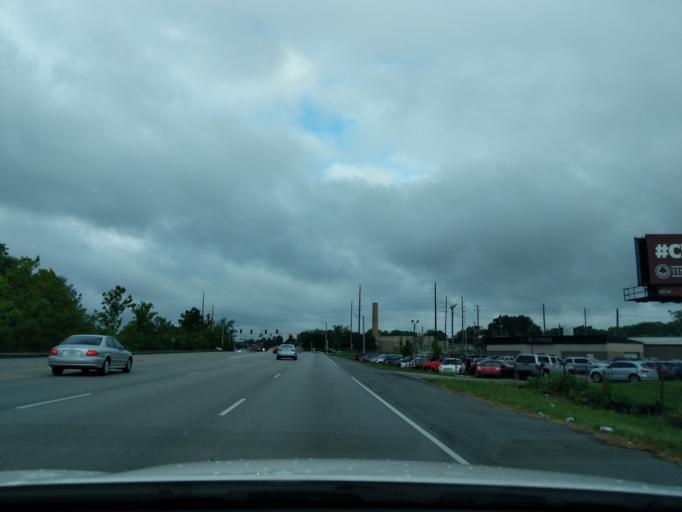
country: US
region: Indiana
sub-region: Marion County
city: Broad Ripple
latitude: 39.8360
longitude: -86.1198
